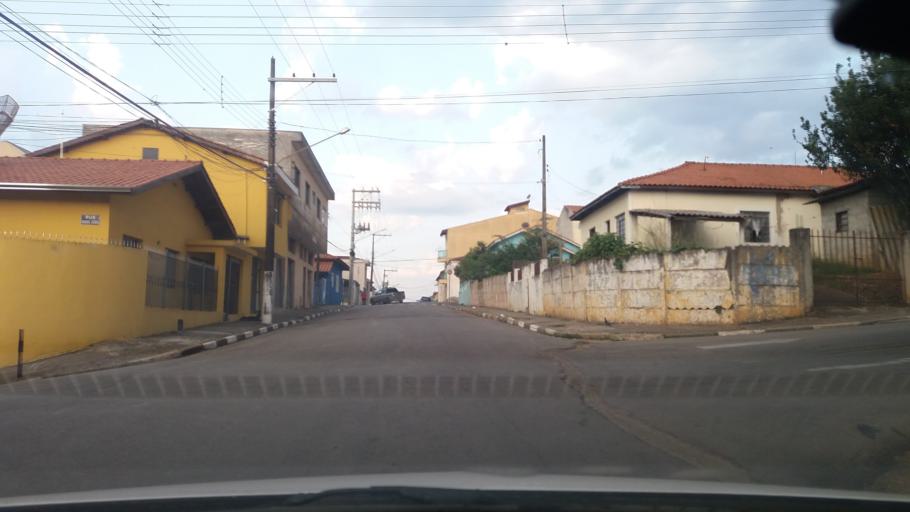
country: BR
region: Sao Paulo
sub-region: Bom Jesus Dos Perdoes
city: Bom Jesus dos Perdoes
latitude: -23.1372
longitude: -46.4656
